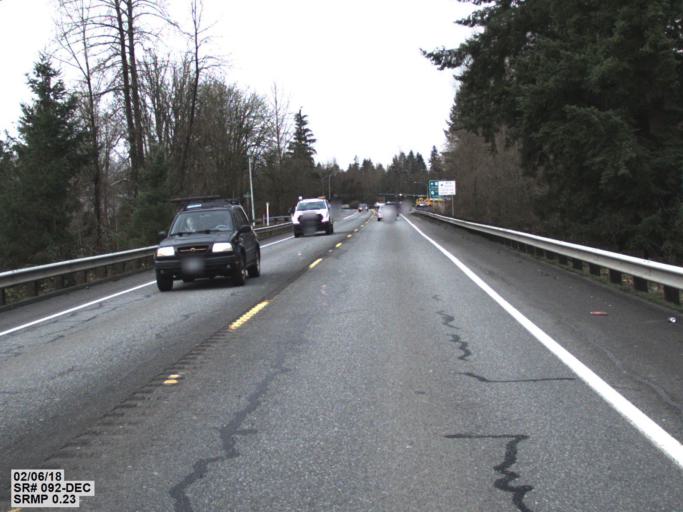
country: US
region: Washington
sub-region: Snohomish County
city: West Lake Stevens
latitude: 48.0283
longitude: -122.1052
